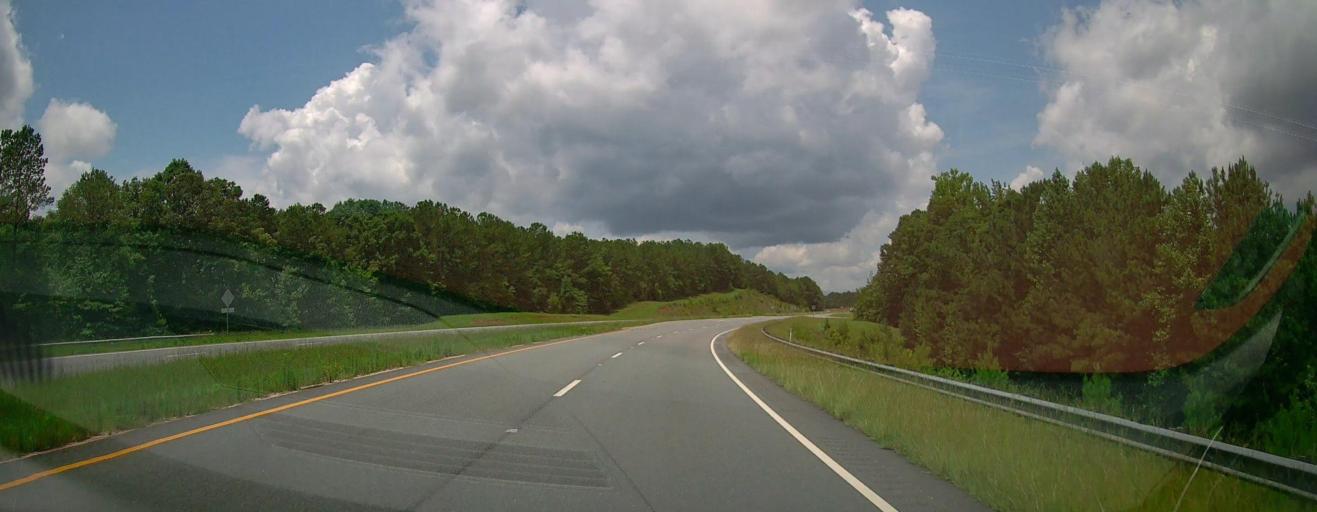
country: US
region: Georgia
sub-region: Upson County
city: Thomaston
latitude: 32.8188
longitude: -84.2964
